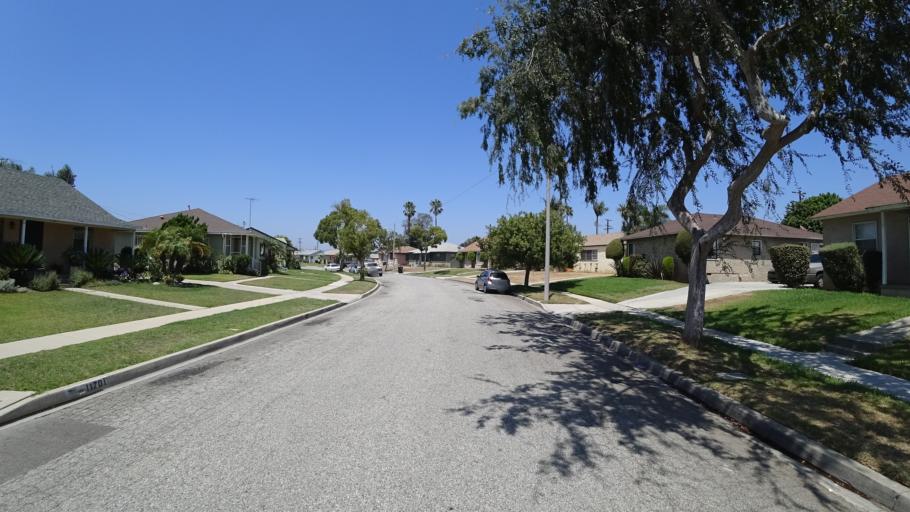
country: US
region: California
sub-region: Los Angeles County
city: West Athens
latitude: 33.9280
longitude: -118.3285
